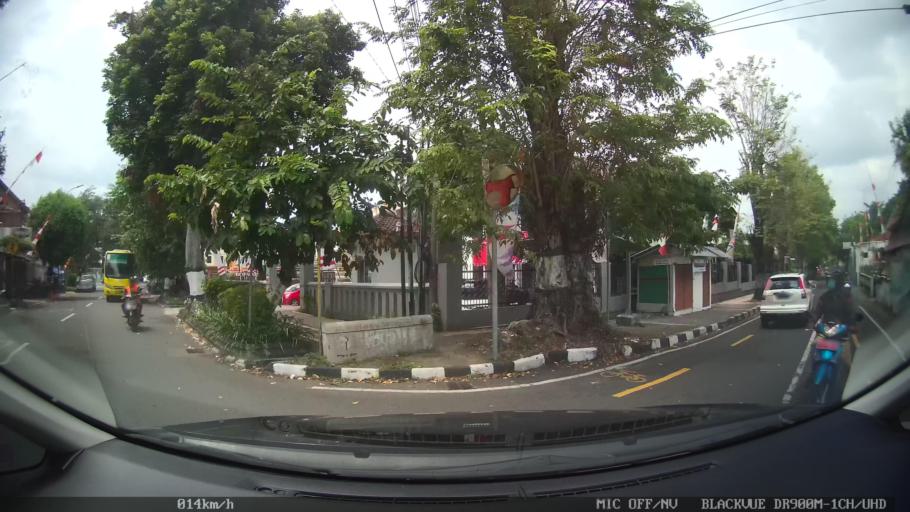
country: ID
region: Daerah Istimewa Yogyakarta
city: Yogyakarta
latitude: -7.7975
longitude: 110.3814
